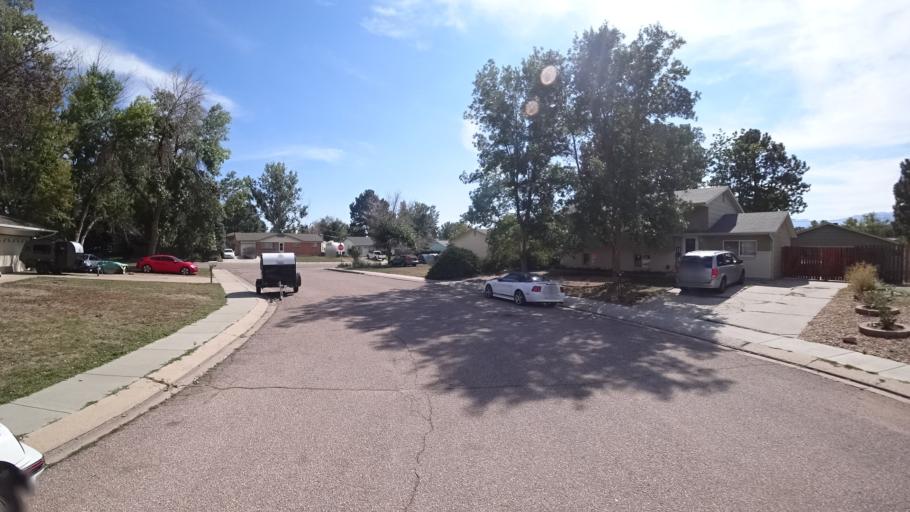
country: US
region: Colorado
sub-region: El Paso County
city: Cimarron Hills
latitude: 38.8933
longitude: -104.7674
